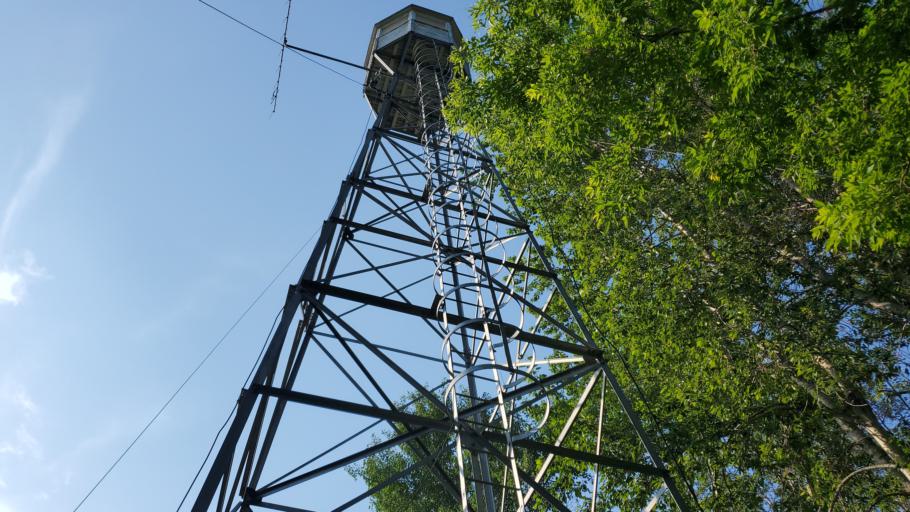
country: CA
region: Ontario
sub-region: Rainy River District
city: Atikokan
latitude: 49.4162
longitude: -91.6661
